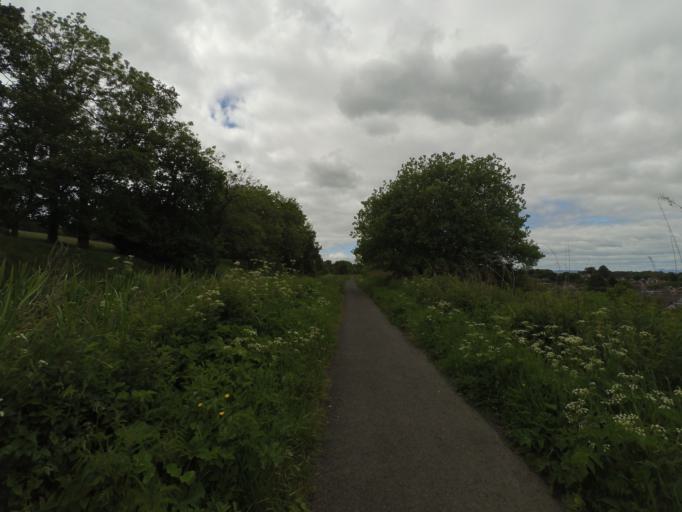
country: GB
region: Scotland
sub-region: Falkirk
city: Polmont
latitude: 55.9832
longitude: -3.7032
